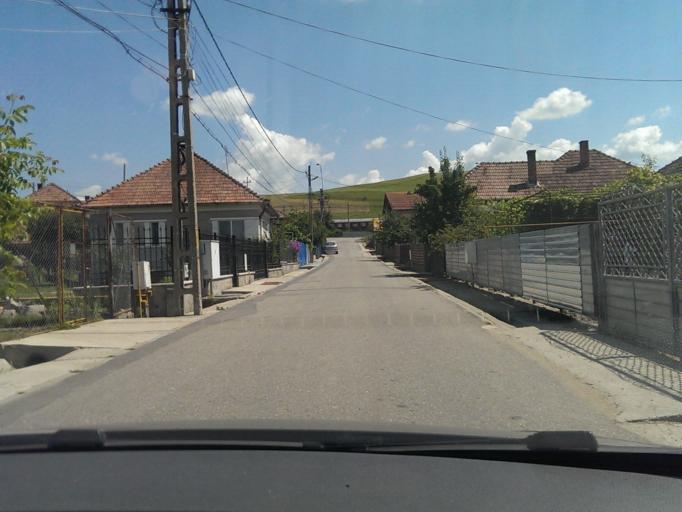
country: RO
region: Cluj
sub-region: Comuna Apahida
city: Sannicoara
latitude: 46.7943
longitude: 23.7460
